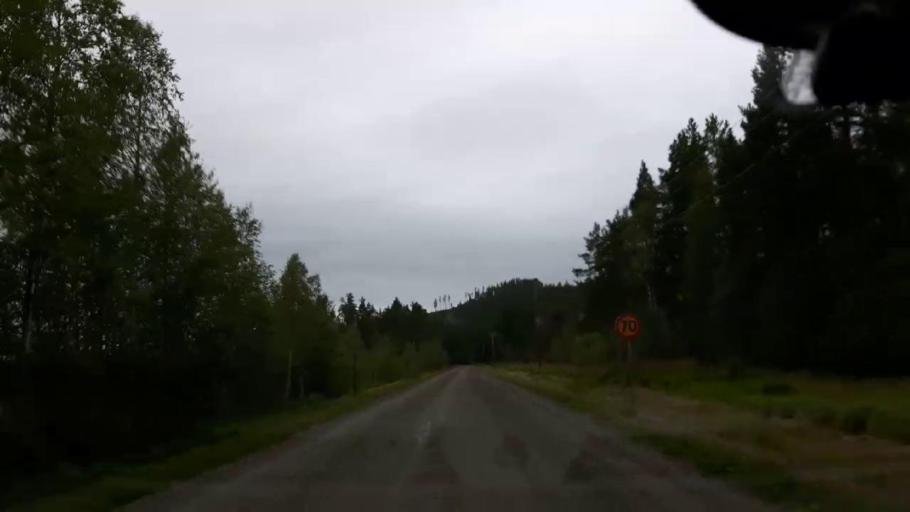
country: SE
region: Vaesternorrland
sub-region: Ange Kommun
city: Fransta
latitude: 62.7841
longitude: 16.0679
